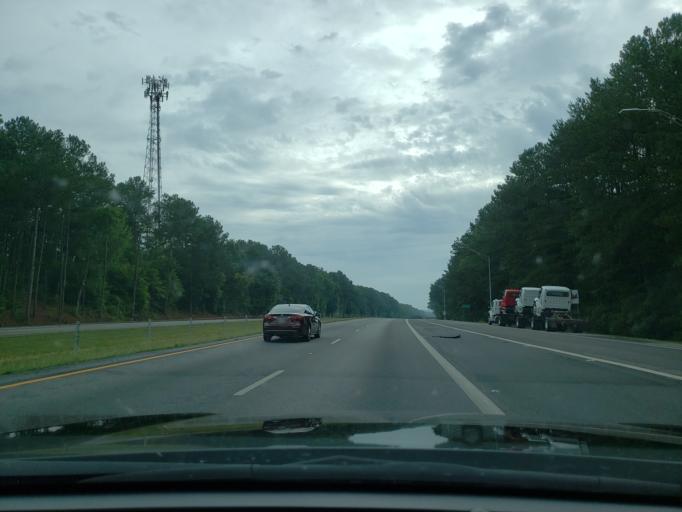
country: US
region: Georgia
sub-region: Troup County
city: West Point
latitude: 32.8616
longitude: -85.1713
